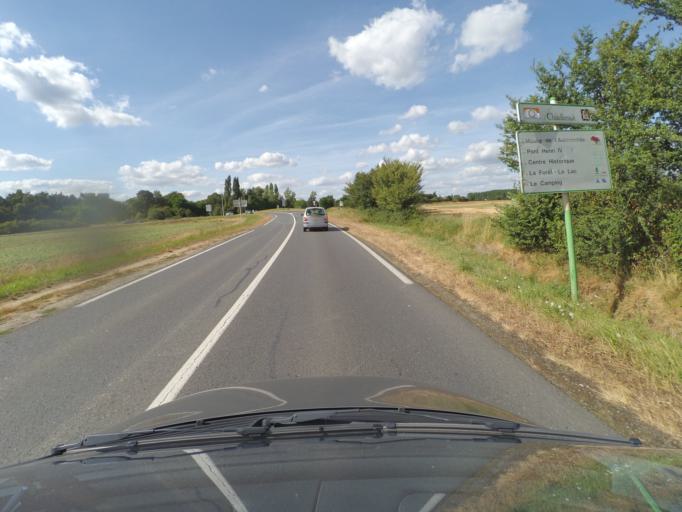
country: FR
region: Poitou-Charentes
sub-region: Departement de la Vienne
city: Cenon-sur-Vienne
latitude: 46.7849
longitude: 0.5475
